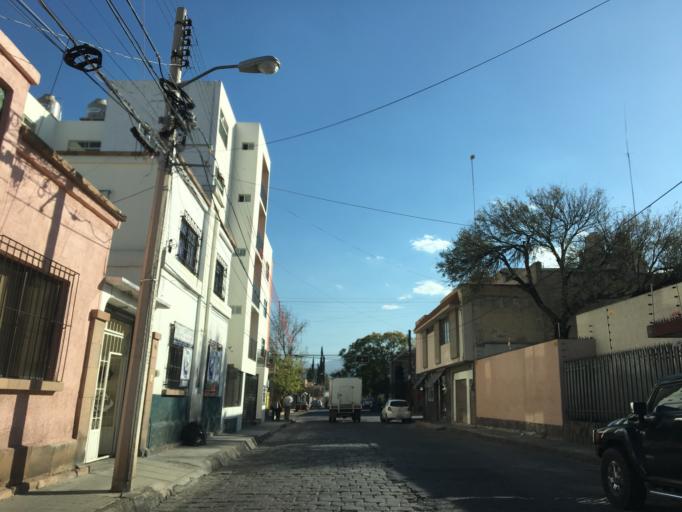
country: MX
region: San Luis Potosi
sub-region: San Luis Potosi
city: San Luis Potosi
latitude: 22.1479
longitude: -100.9927
